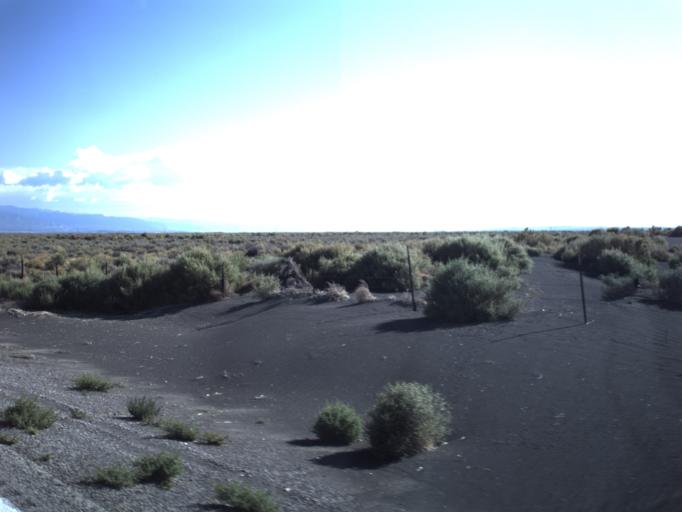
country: US
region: Utah
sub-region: Millard County
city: Delta
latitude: 39.2612
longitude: -112.4470
